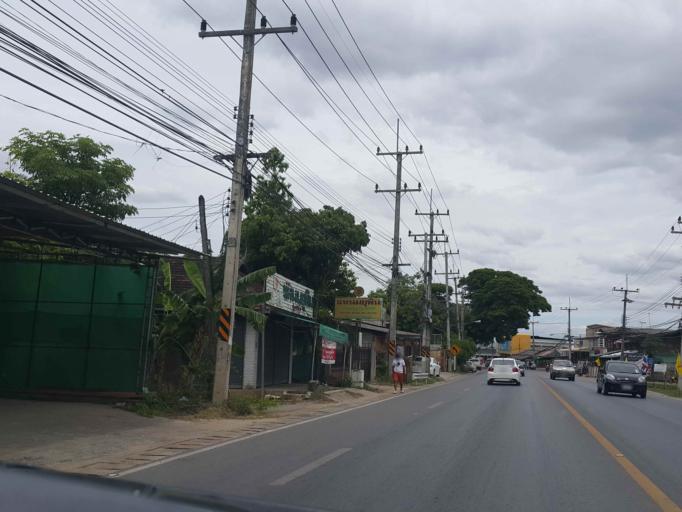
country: TH
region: Chiang Mai
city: San Pa Tong
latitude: 18.5632
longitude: 98.8700
